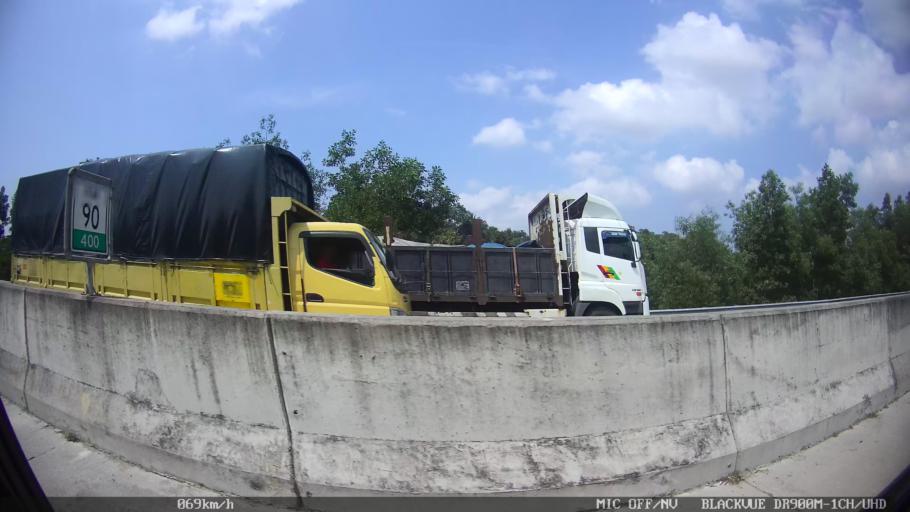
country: ID
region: Lampung
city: Natar
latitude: -5.3046
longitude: 105.2454
